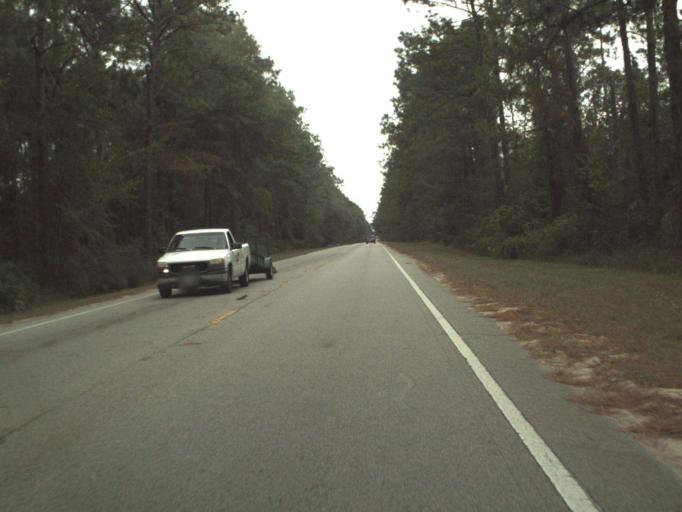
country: US
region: Florida
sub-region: Leon County
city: Woodville
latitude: 30.3068
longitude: -84.3118
